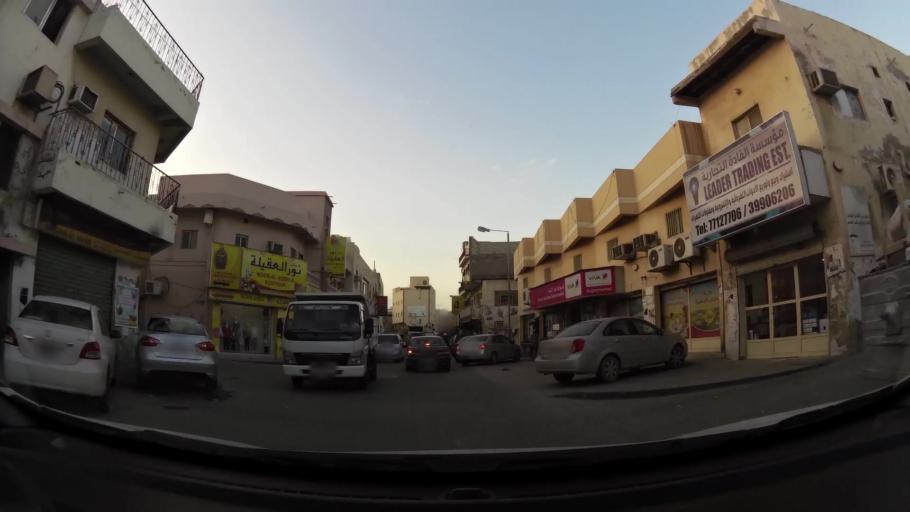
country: BH
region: Manama
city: Jidd Hafs
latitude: 26.2225
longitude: 50.5356
